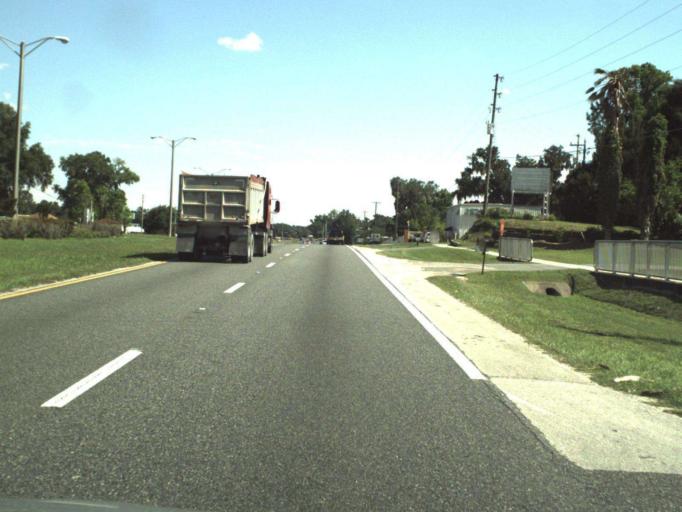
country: US
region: Florida
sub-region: Marion County
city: Belleview
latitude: 29.0687
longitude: -82.0703
